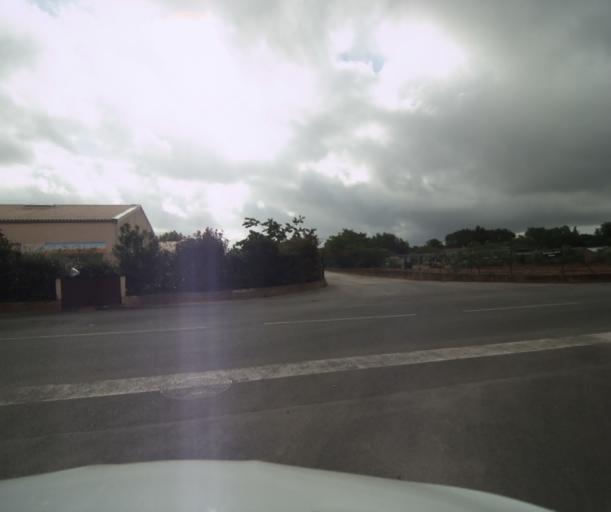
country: FR
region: Provence-Alpes-Cote d'Azur
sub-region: Departement du Var
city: Ollioules
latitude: 43.1267
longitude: 5.8591
